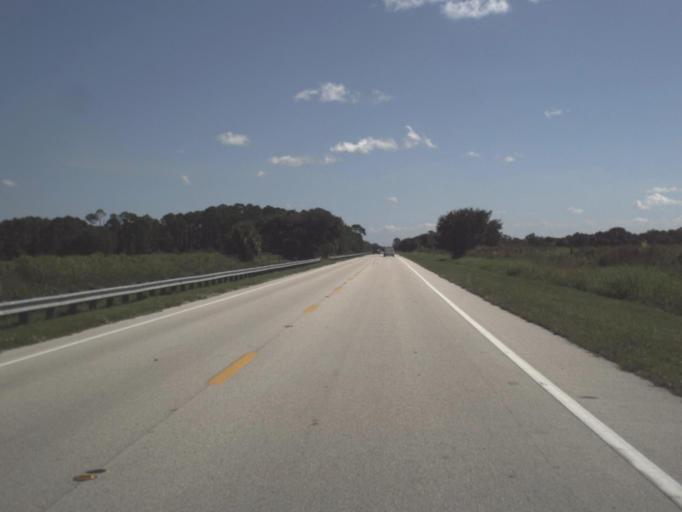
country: US
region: Florida
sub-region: Hendry County
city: Port LaBelle
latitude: 26.8123
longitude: -81.3763
